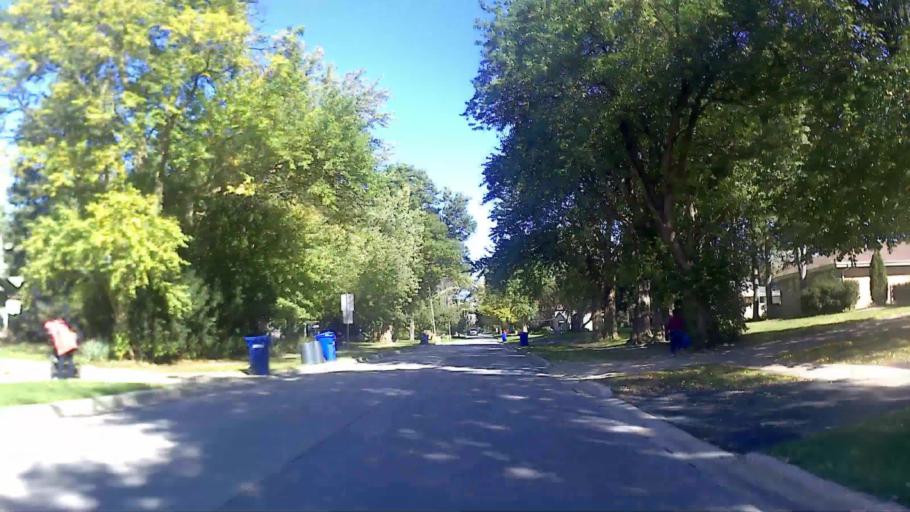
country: US
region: Illinois
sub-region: DuPage County
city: Glen Ellyn
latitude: 41.8657
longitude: -88.0812
